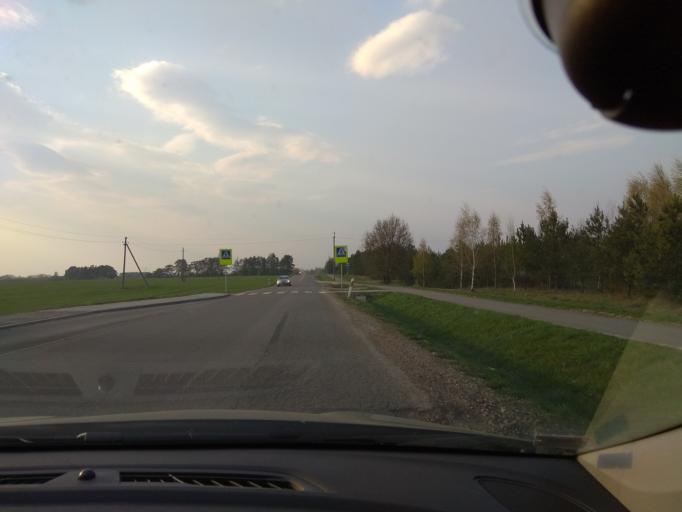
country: LT
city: Grigiskes
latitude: 54.6169
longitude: 25.1170
